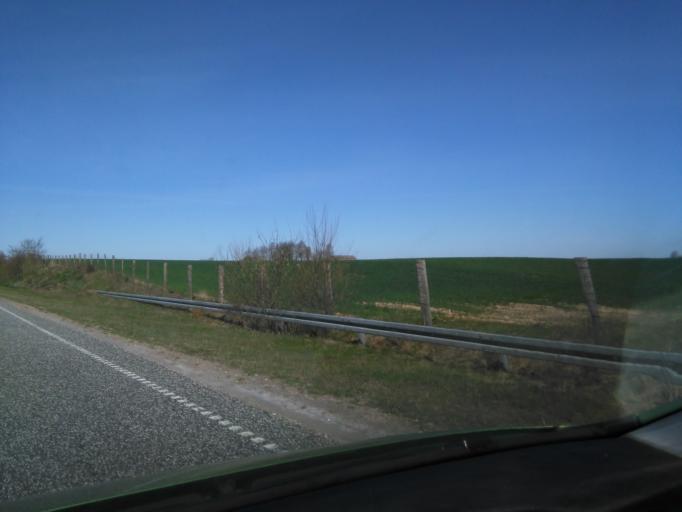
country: DK
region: Central Jutland
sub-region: Hedensted Kommune
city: Hedensted
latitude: 55.8421
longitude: 9.6861
